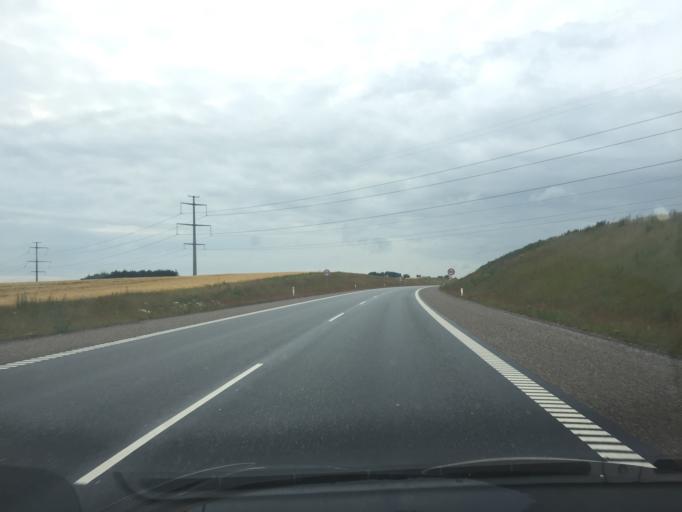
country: DK
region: Capital Region
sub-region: Egedal Kommune
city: Smorumnedre
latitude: 55.7261
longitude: 12.2851
